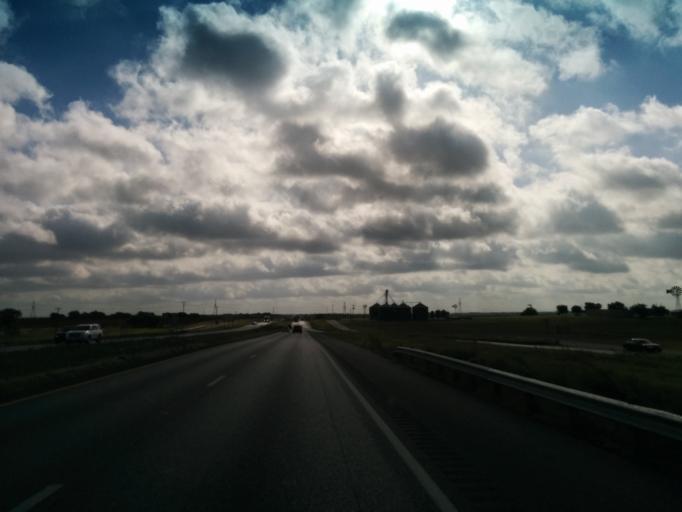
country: US
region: Texas
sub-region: Guadalupe County
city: McQueeney
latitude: 29.5405
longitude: -98.0717
